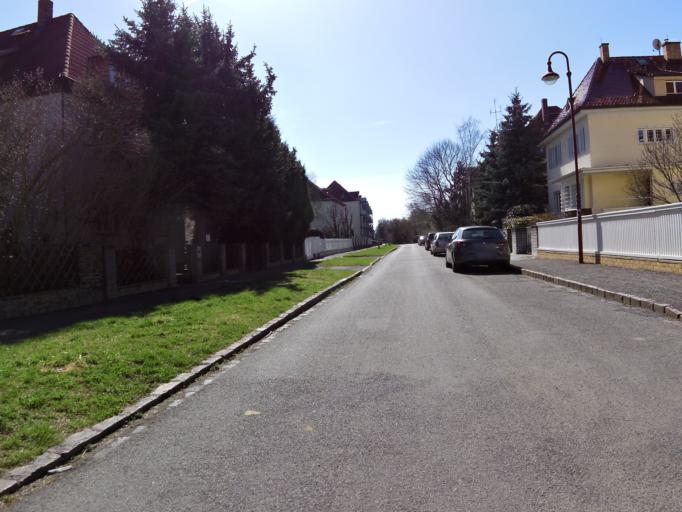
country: DE
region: Saxony
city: Markkleeberg
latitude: 51.2792
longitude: 12.3946
